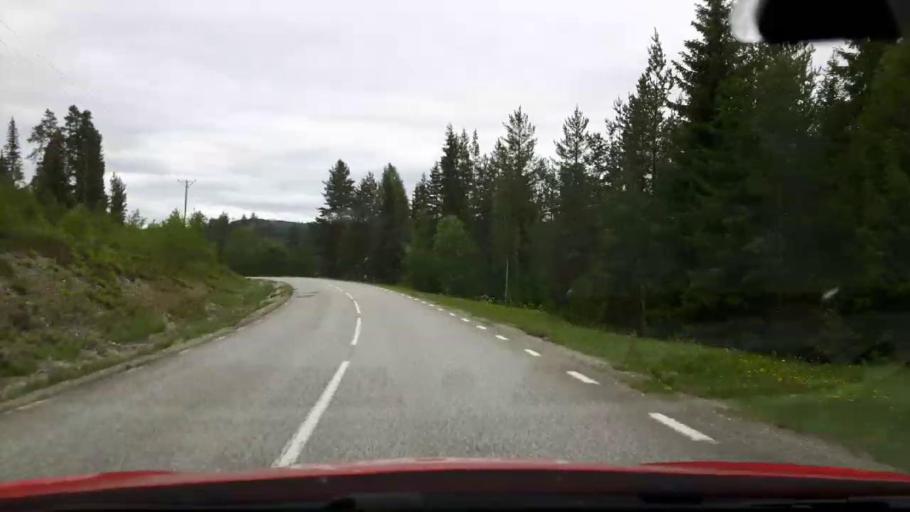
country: SE
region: Jaemtland
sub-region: Stroemsunds Kommun
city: Stroemsund
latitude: 63.2936
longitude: 15.7708
